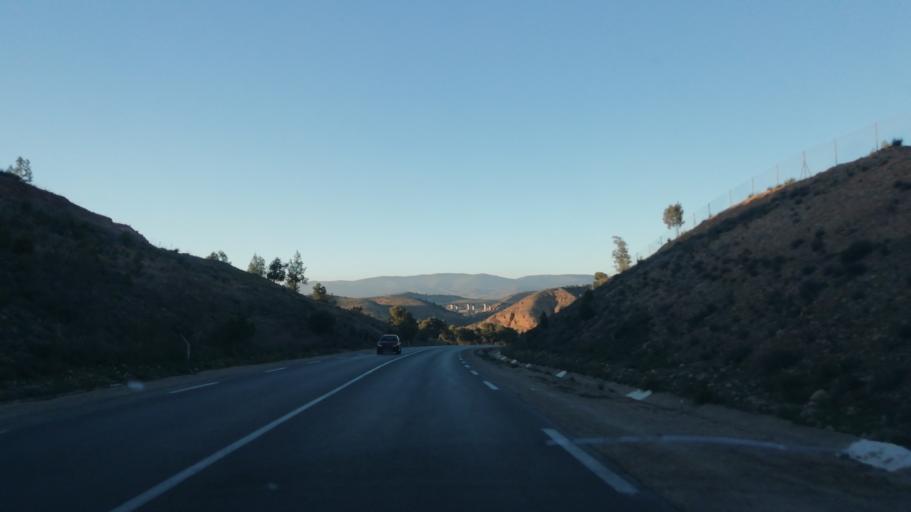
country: DZ
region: Tlemcen
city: Nedroma
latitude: 34.8811
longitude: -1.6700
